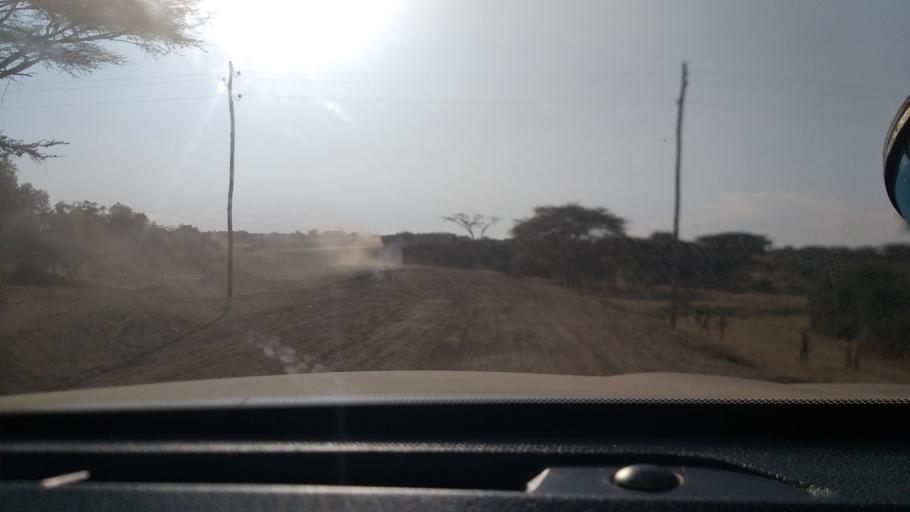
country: ET
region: Oromiya
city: Shashemene
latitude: 7.4885
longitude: 38.7276
